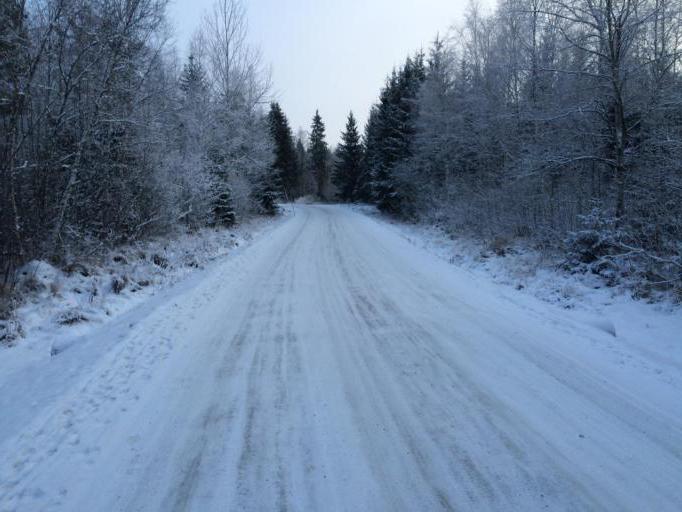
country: SE
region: Uppsala
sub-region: Enkopings Kommun
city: Orsundsbro
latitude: 59.9092
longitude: 17.1930
